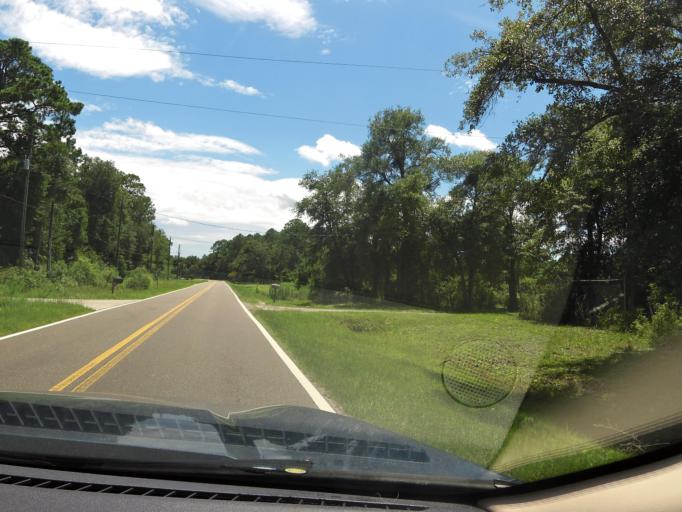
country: US
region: Georgia
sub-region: Camden County
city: St. Marys
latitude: 30.6703
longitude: -81.5324
